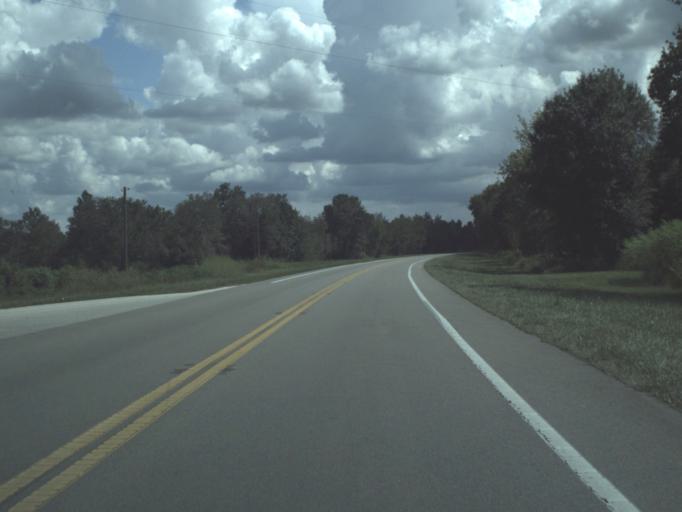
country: US
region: Florida
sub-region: Polk County
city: Kathleen
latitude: 28.2044
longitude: -82.0072
